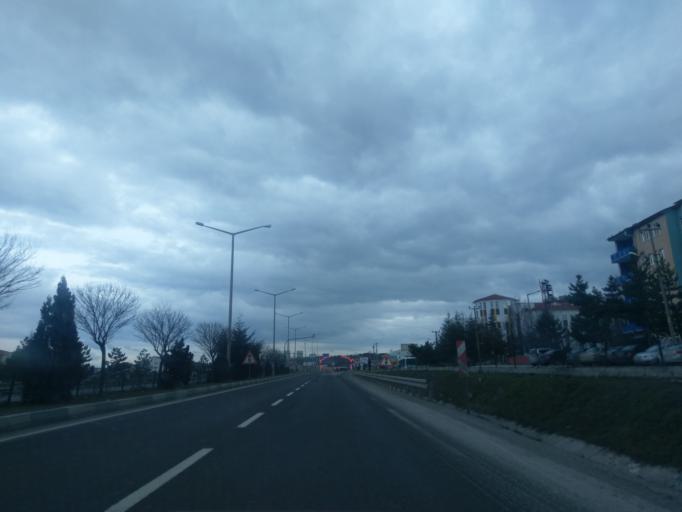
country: TR
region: Kuetahya
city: Kutahya
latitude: 39.3857
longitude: 30.0415
